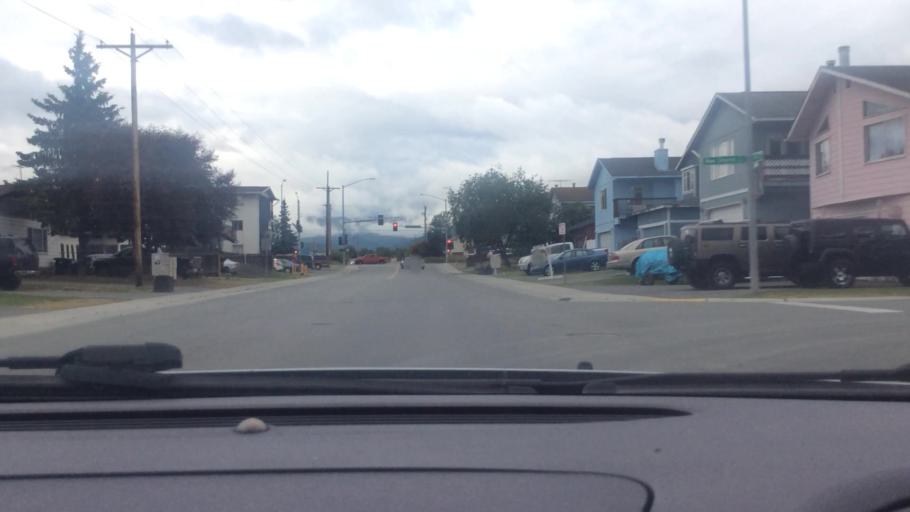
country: US
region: Alaska
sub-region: Anchorage Municipality
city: Anchorage
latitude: 61.2187
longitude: -149.7812
